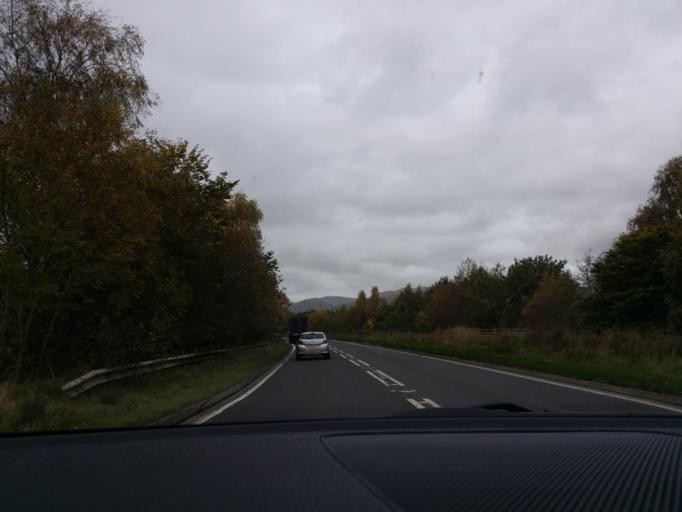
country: GB
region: Scotland
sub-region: Clackmannanshire
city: Clackmannan
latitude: 56.1102
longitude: -3.7439
